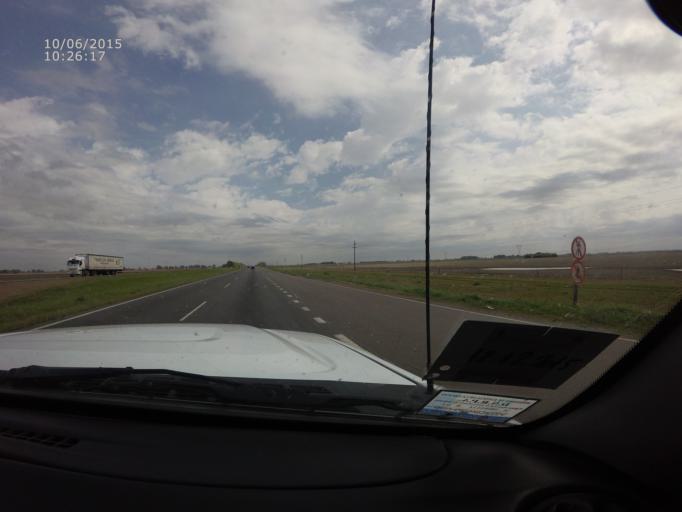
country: AR
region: Buenos Aires
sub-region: Partido de Ramallo
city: Ramallo
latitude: -33.6808
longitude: -59.9287
